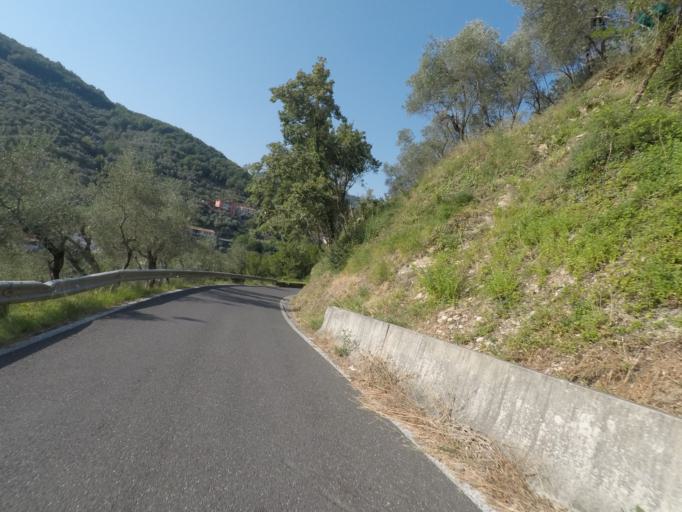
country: IT
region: Liguria
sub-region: Provincia di La Spezia
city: Casano-Dogana-Isola
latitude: 44.0913
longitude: 10.0495
